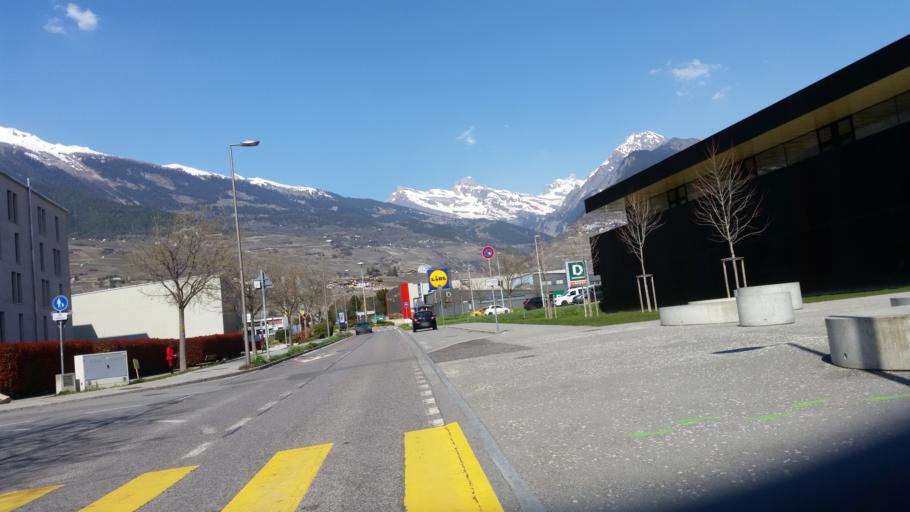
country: CH
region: Valais
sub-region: Conthey District
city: Conthey
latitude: 46.2221
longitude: 7.3036
